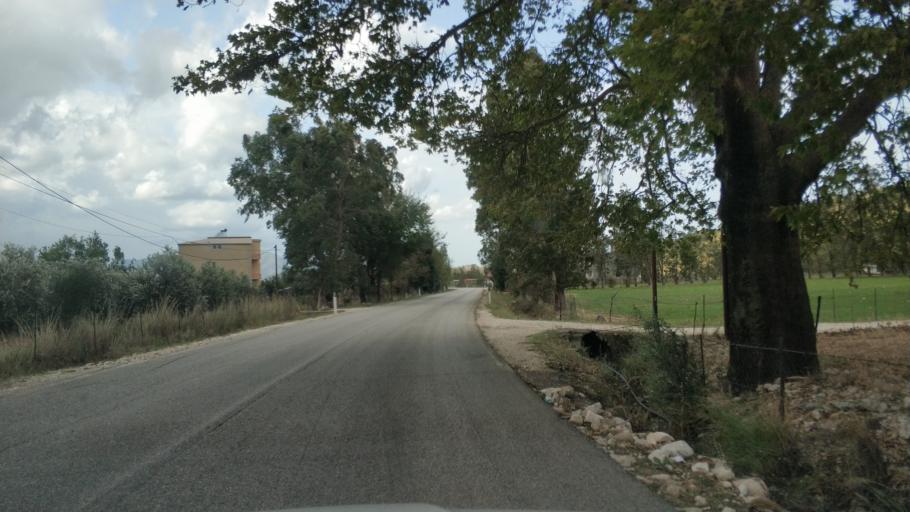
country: AL
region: Vlore
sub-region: Rrethi i Vlores
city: Orikum
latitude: 40.2789
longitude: 19.5033
